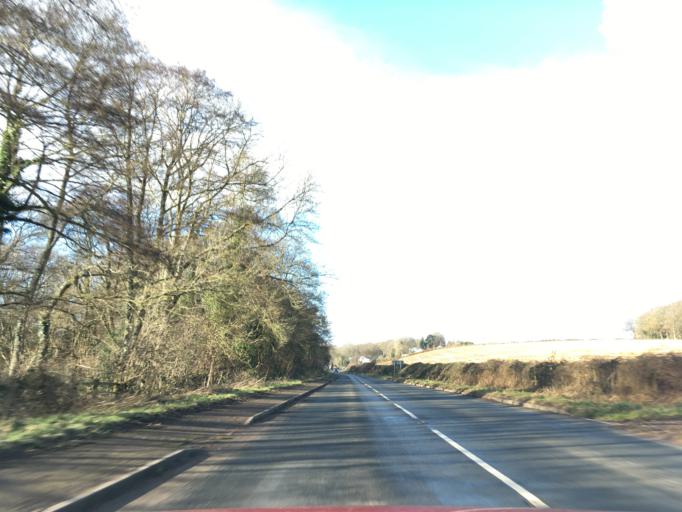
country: GB
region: Wales
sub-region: Monmouthshire
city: Usk
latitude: 51.7165
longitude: -2.9288
